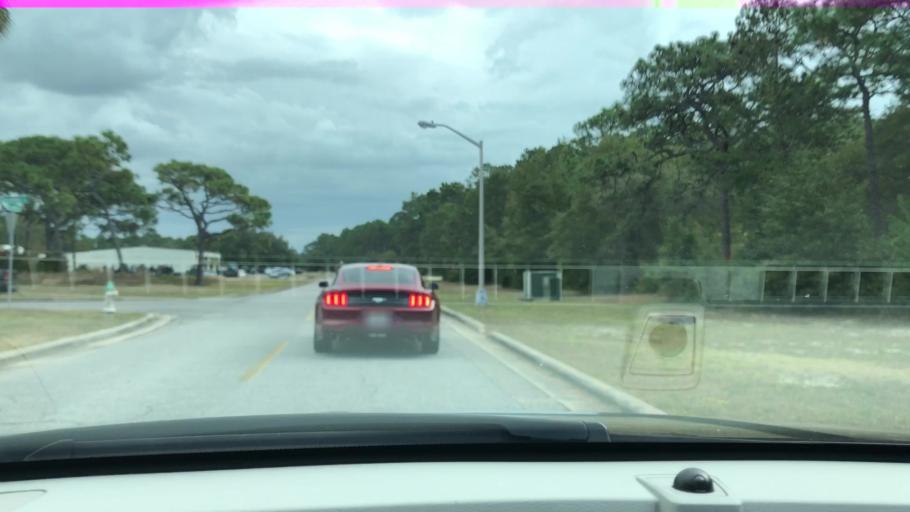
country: US
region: Florida
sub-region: Bay County
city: Tyndall Air Force Base
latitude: 30.0608
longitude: -85.5871
